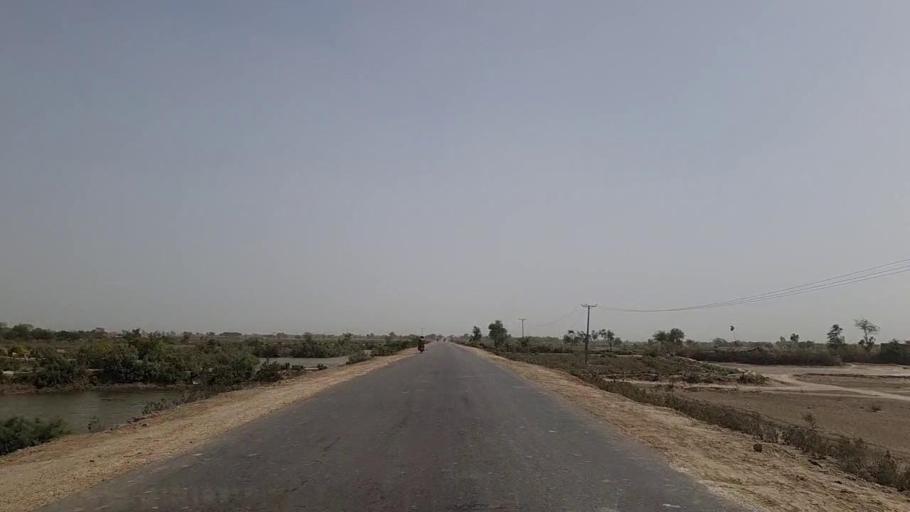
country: PK
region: Sindh
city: Talhar
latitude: 24.8672
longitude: 68.8441
